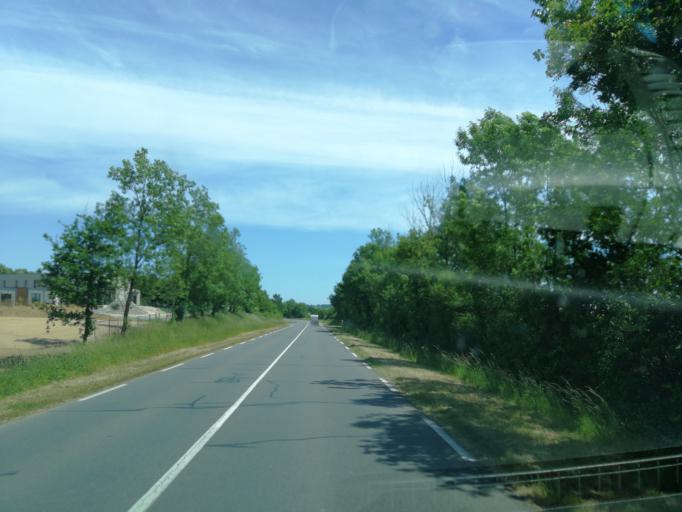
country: FR
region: Pays de la Loire
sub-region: Departement de la Vendee
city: La Chataigneraie
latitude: 46.6397
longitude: -0.7491
